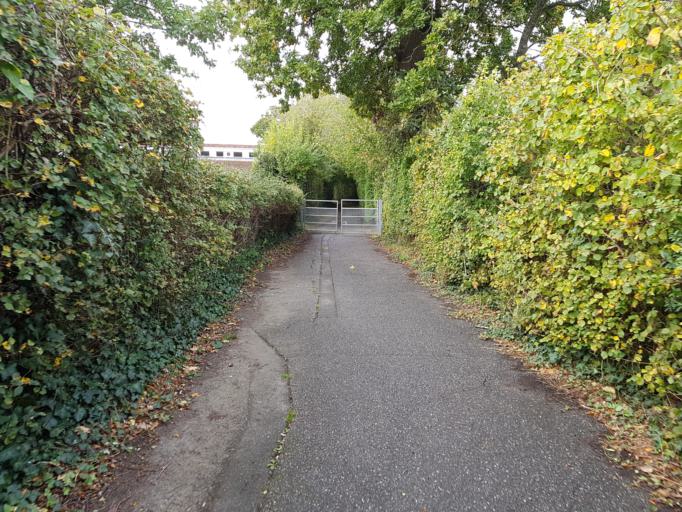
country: GB
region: England
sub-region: Isle of Wight
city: Ryde
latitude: 50.7291
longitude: -1.1760
